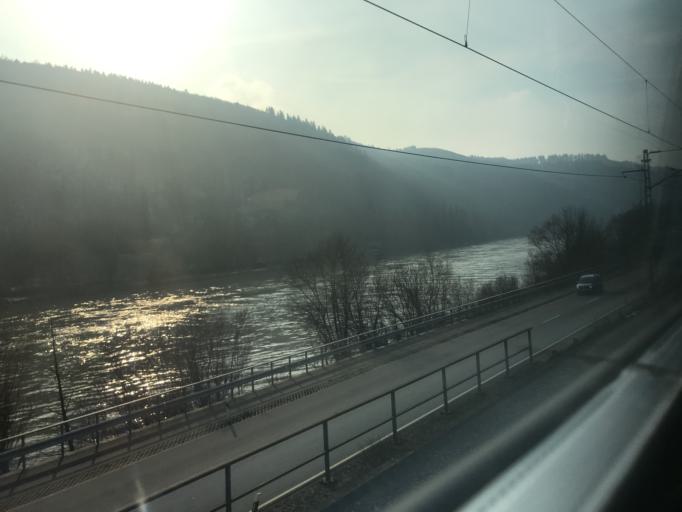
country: DE
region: Rheinland-Pfalz
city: Klotten
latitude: 50.1676
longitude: 7.2079
